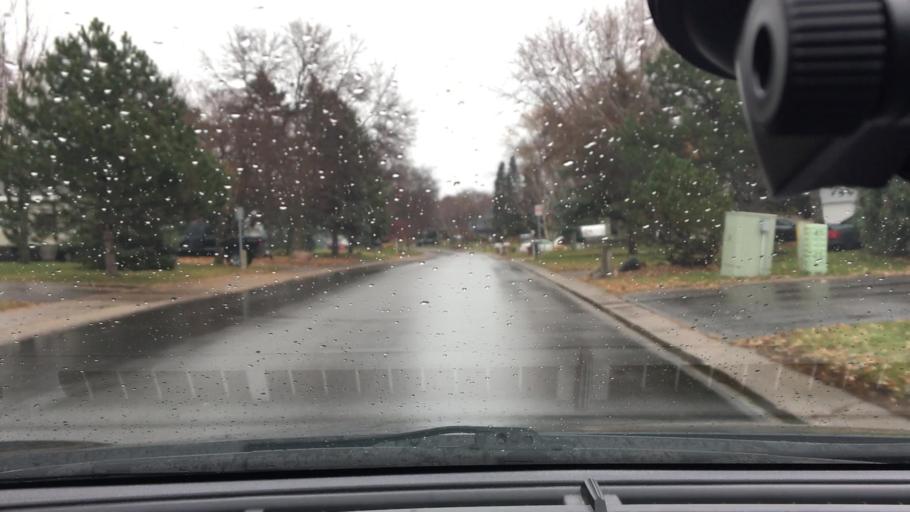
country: US
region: Minnesota
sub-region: Hennepin County
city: Corcoran
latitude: 45.1116
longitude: -93.5106
